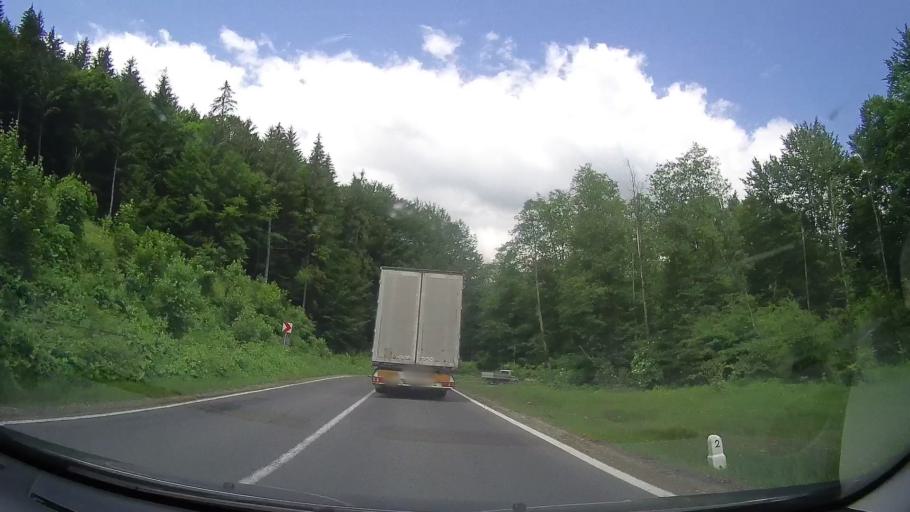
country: RO
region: Prahova
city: Maneciu
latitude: 45.3819
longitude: 25.9289
